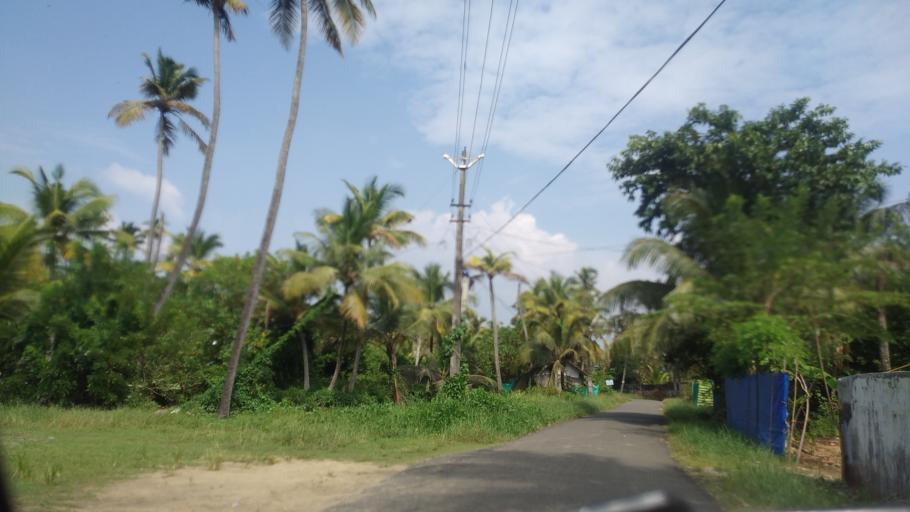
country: IN
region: Kerala
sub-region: Ernakulam
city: Elur
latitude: 10.0865
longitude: 76.1985
